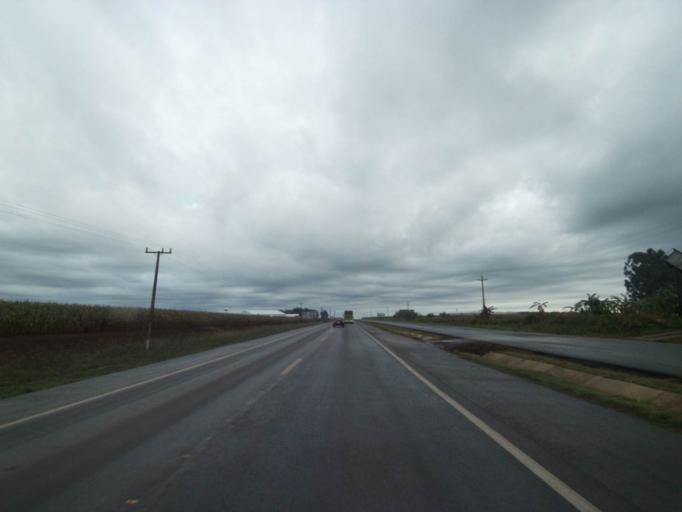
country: BR
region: Parana
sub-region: Toledo
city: Toledo
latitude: -24.6848
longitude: -53.7758
